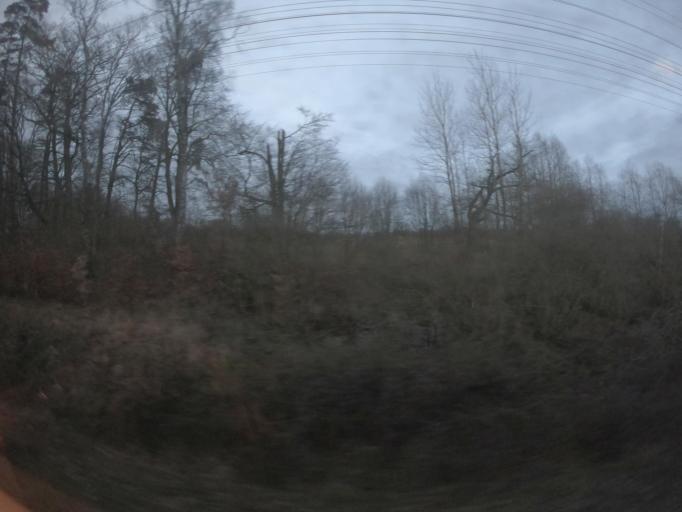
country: PL
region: West Pomeranian Voivodeship
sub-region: Powiat drawski
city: Wierzchowo
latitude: 53.5257
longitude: 16.1357
